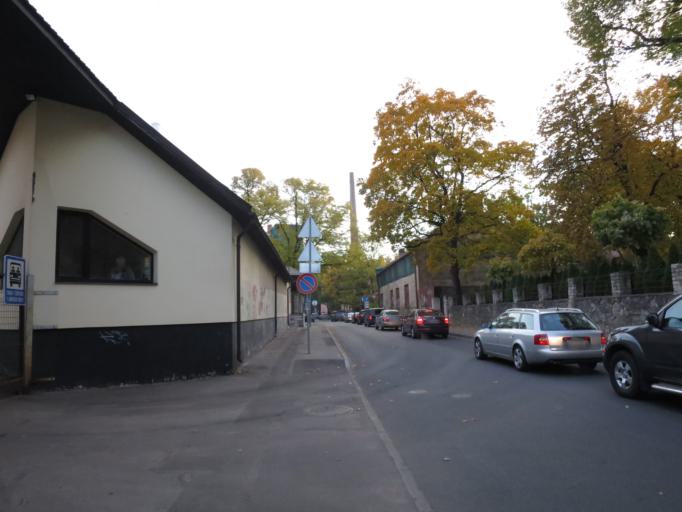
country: LV
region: Riga
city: Riga
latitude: 56.9638
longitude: 24.1284
